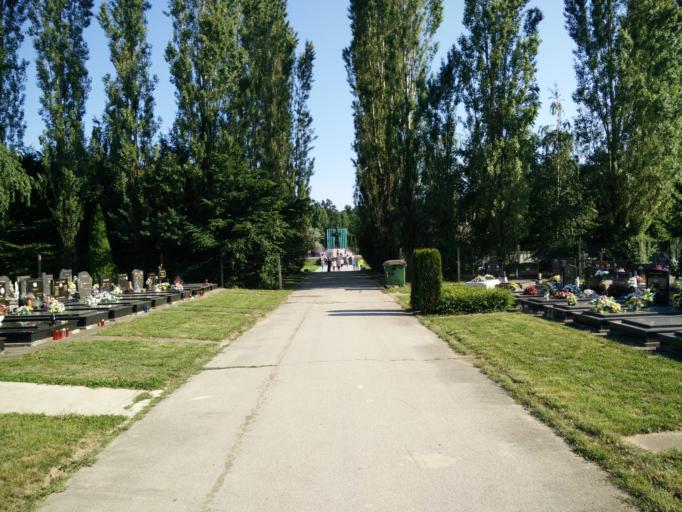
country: HR
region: Vukovarsko-Srijemska
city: Vukovar
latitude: 45.3287
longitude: 19.0387
